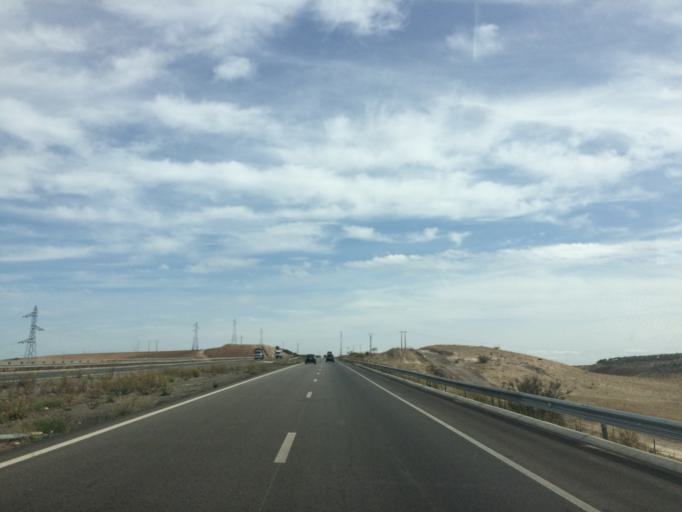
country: MA
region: Meknes-Tafilalet
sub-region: Meknes
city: Meknes
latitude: 33.8824
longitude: -5.7554
